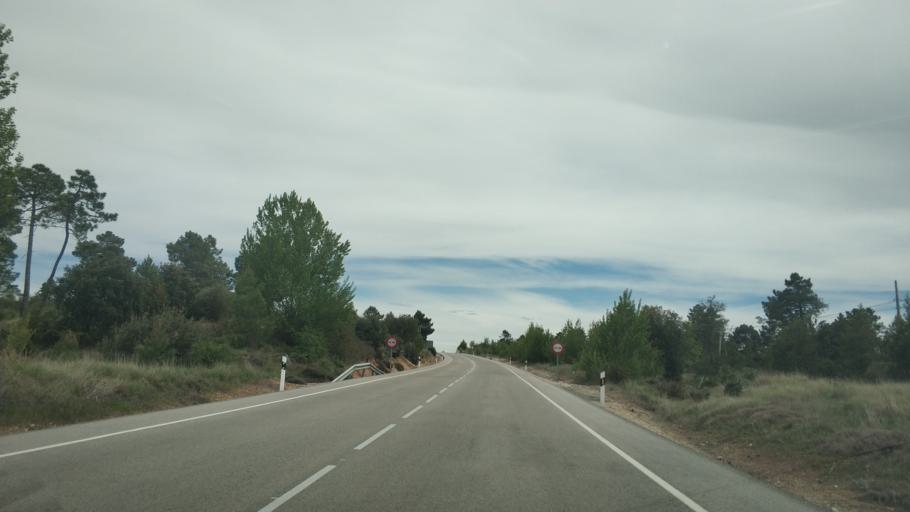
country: ES
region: Castille and Leon
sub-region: Provincia de Soria
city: Valdenebro
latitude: 41.5459
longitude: -2.9594
